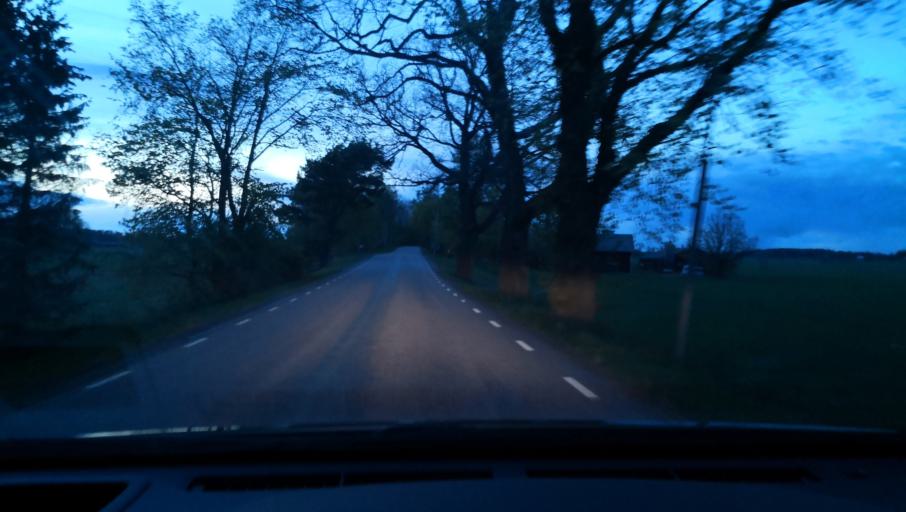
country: SE
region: OErebro
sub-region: Askersunds Kommun
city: Asbro
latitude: 59.0809
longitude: 15.0067
